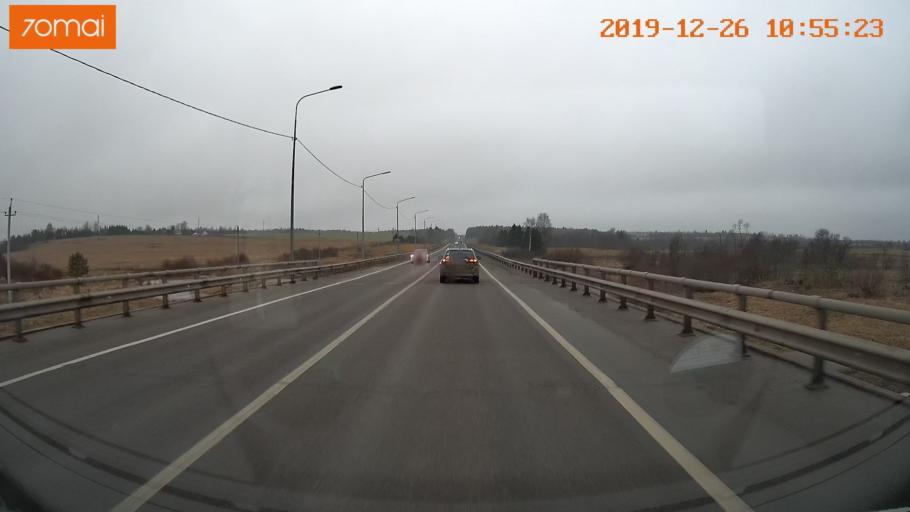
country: RU
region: Vologda
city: Molochnoye
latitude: 59.1893
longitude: 39.5838
